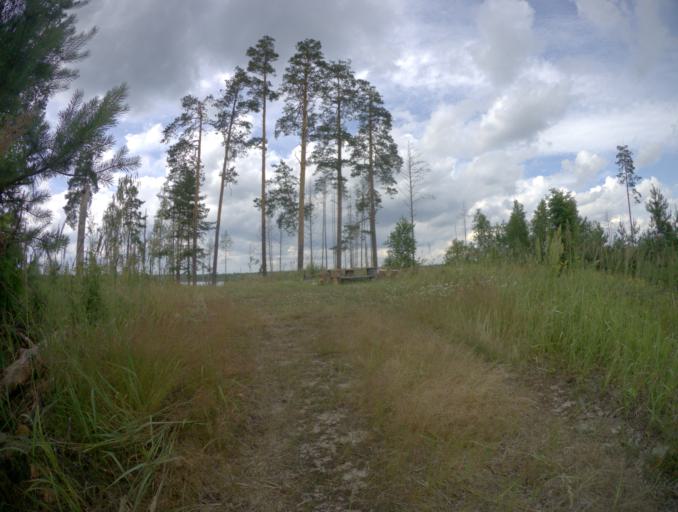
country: RU
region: Vladimir
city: Gorokhovets
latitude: 56.3023
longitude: 42.7010
